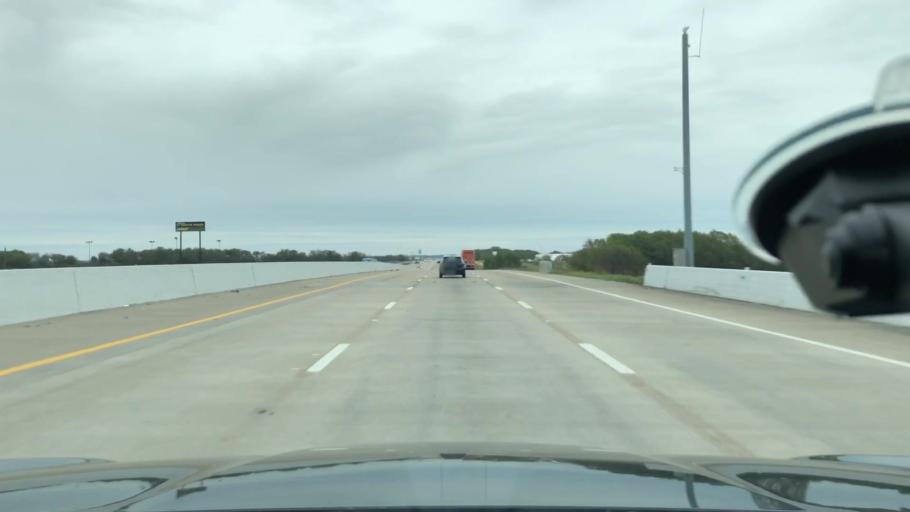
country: US
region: Texas
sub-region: Ellis County
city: Italy
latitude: 32.1960
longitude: -96.8992
